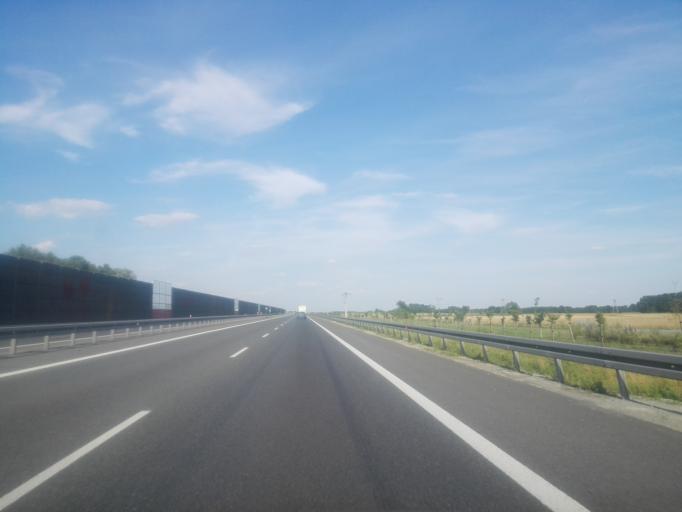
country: PL
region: Lower Silesian Voivodeship
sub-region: Powiat wroclawski
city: Dlugoleka
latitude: 51.2264
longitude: 17.2131
